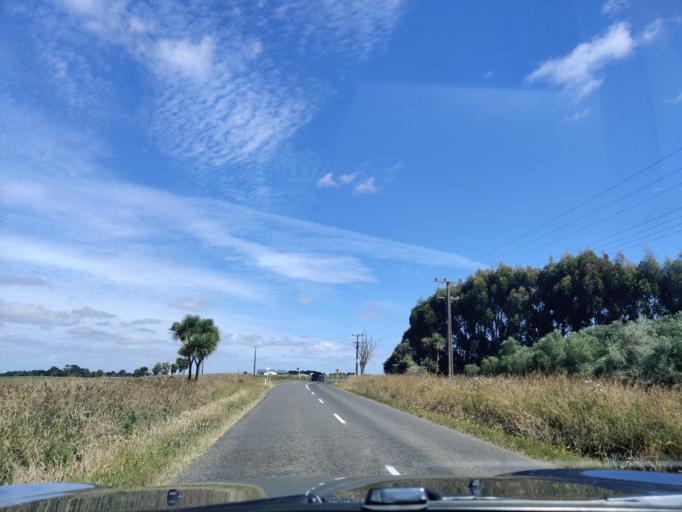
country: NZ
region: Manawatu-Wanganui
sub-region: Rangitikei District
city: Bulls
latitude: -40.1935
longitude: 175.4764
